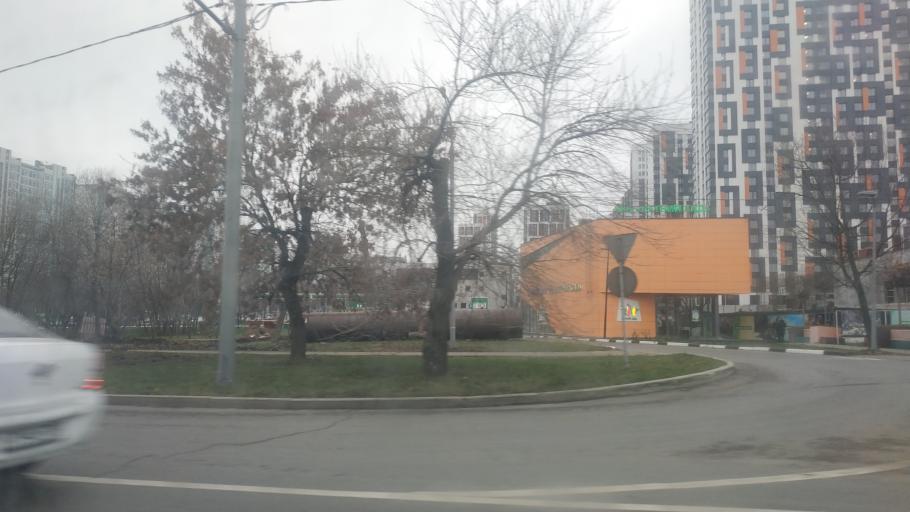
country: RU
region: Moskovskaya
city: Vostochnoe Degunino
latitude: 55.8792
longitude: 37.5454
